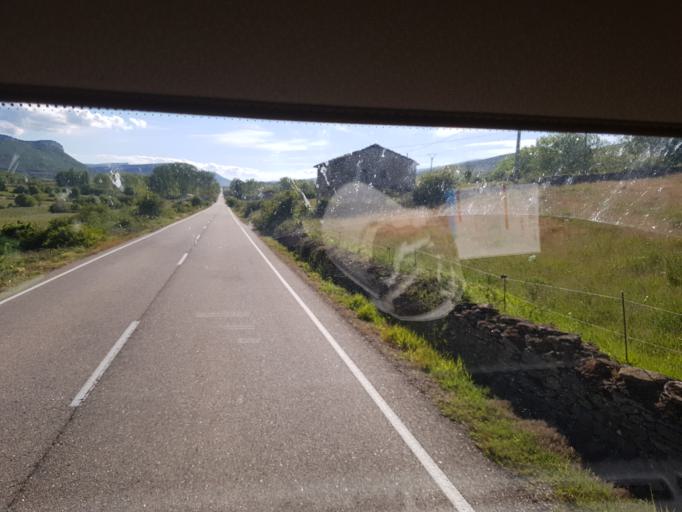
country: ES
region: Castille and Leon
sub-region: Provincia de Burgos
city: Espinosa de los Monteros
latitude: 43.0657
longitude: -3.5729
